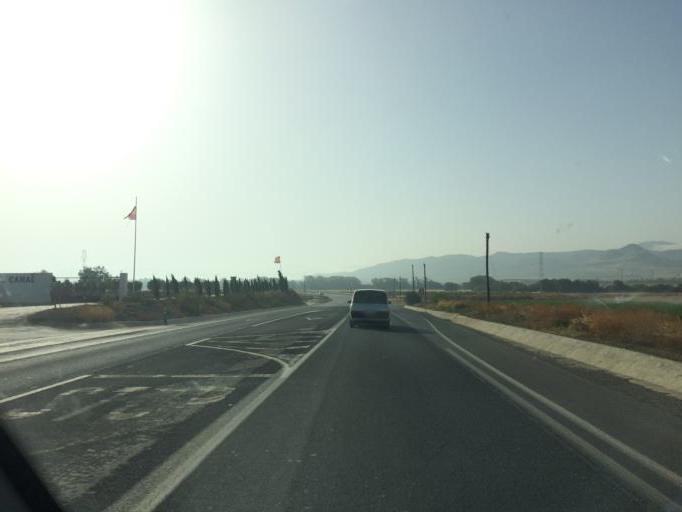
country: ES
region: Andalusia
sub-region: Provincia de Malaga
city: Mollina
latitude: 37.0520
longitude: -4.6573
